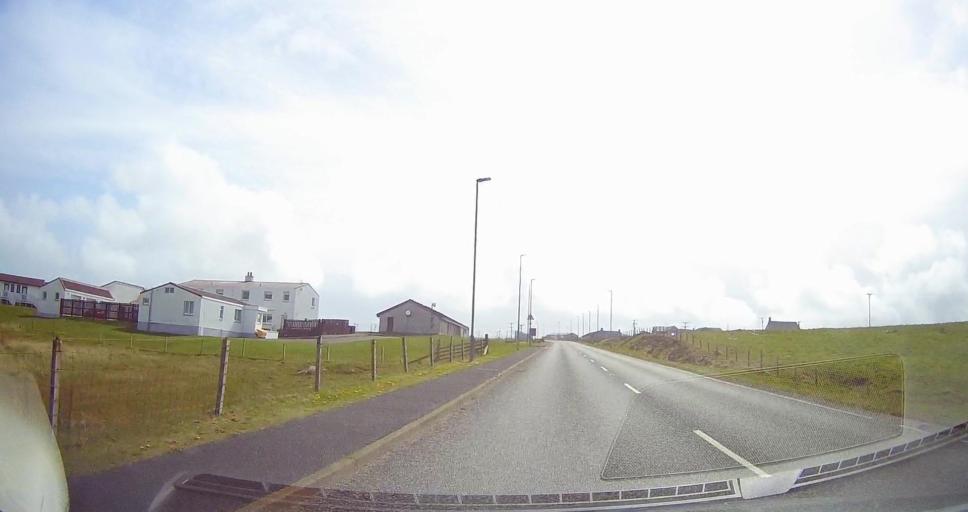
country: GB
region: Scotland
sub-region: Shetland Islands
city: Sandwick
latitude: 59.9229
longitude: -1.2983
